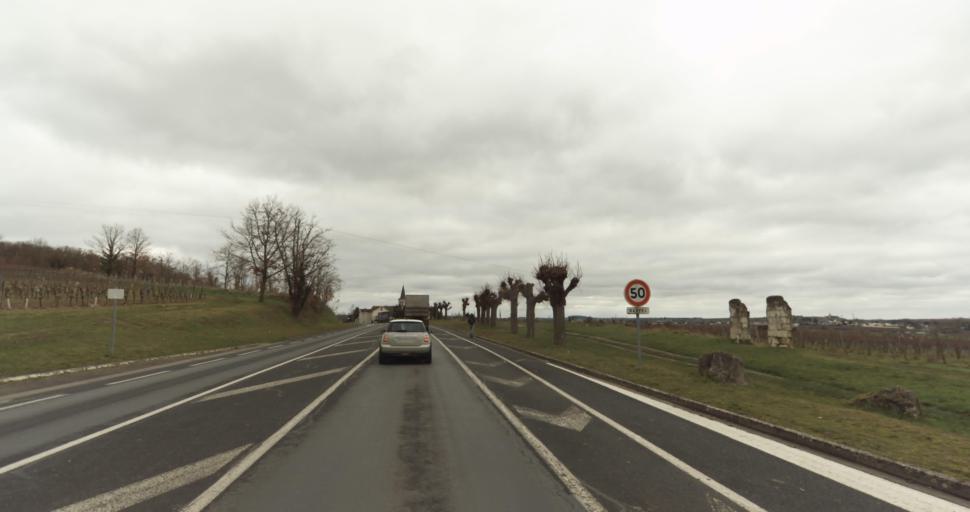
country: FR
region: Pays de la Loire
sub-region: Departement de Maine-et-Loire
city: Varrains
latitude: 47.2290
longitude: -0.0704
